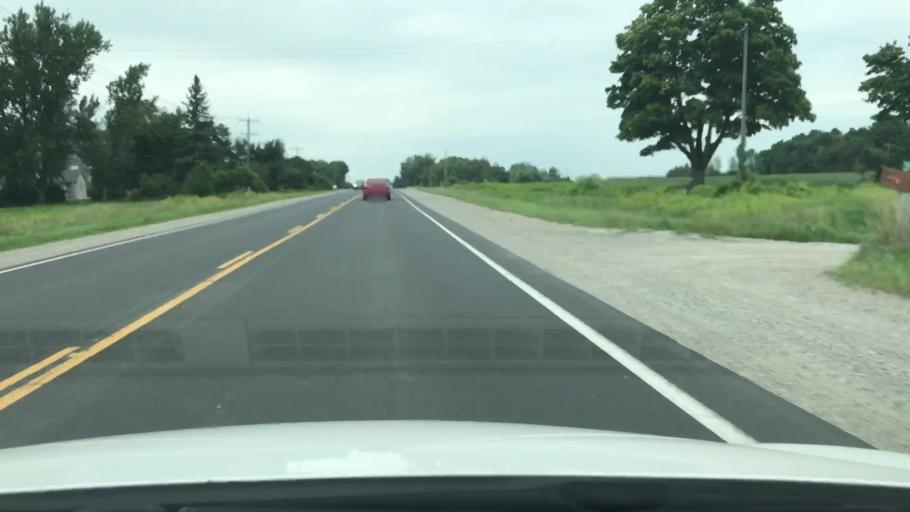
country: CA
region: Ontario
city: Bradford West Gwillimbury
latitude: 44.1784
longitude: -79.5805
